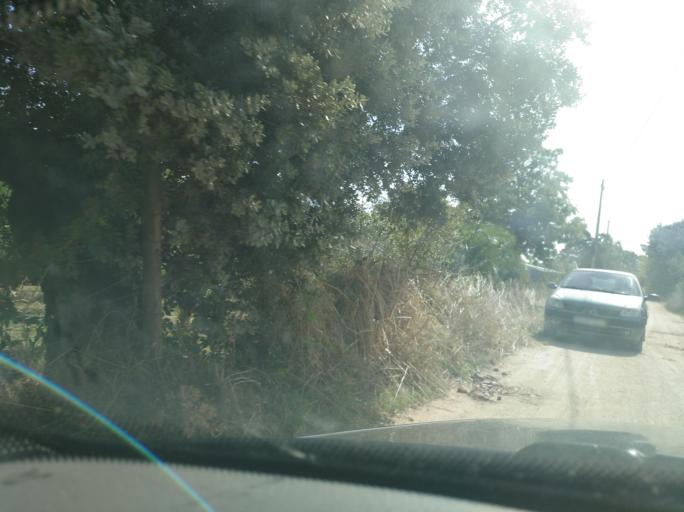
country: PT
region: Portalegre
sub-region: Campo Maior
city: Campo Maior
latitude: 39.0401
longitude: -7.0546
